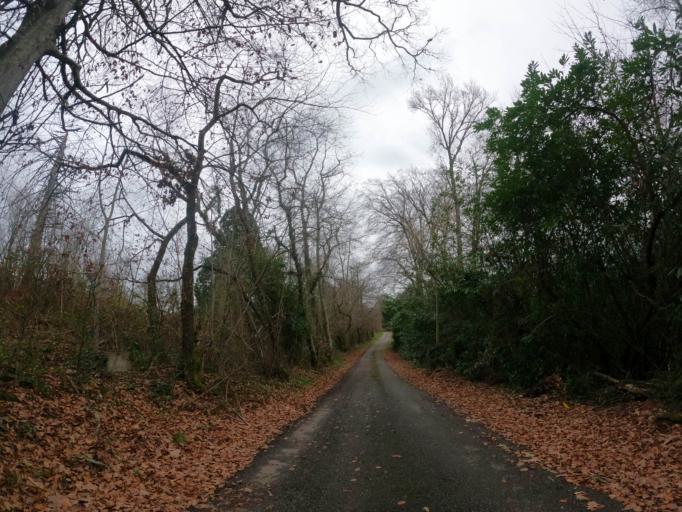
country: FR
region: Aquitaine
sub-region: Departement des Pyrenees-Atlantiques
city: Mazeres-Lezons
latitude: 43.2649
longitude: -0.3512
